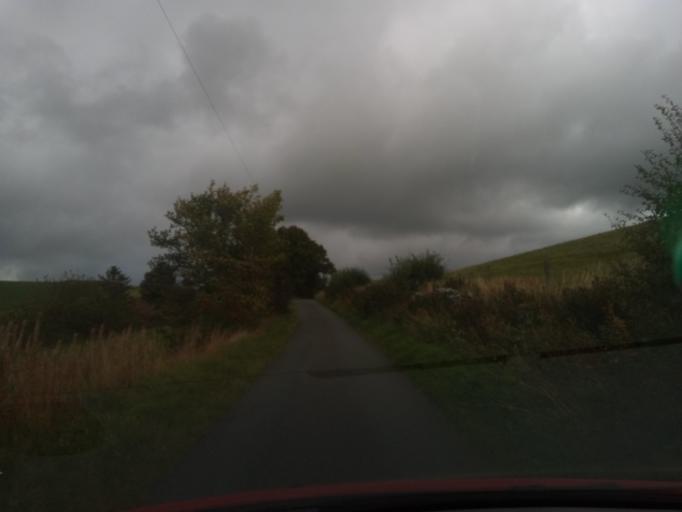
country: GB
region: Scotland
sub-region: The Scottish Borders
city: Coldstream
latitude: 55.5451
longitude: -2.2668
